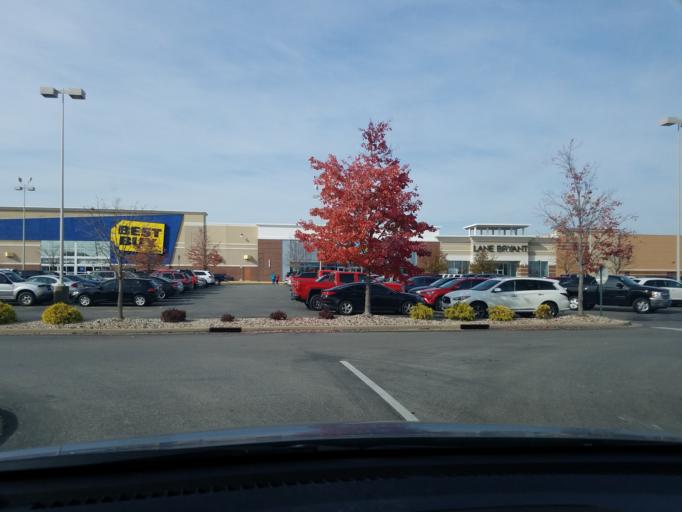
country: US
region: Indiana
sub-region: Clark County
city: Clarksville
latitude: 38.3263
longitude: -85.7654
